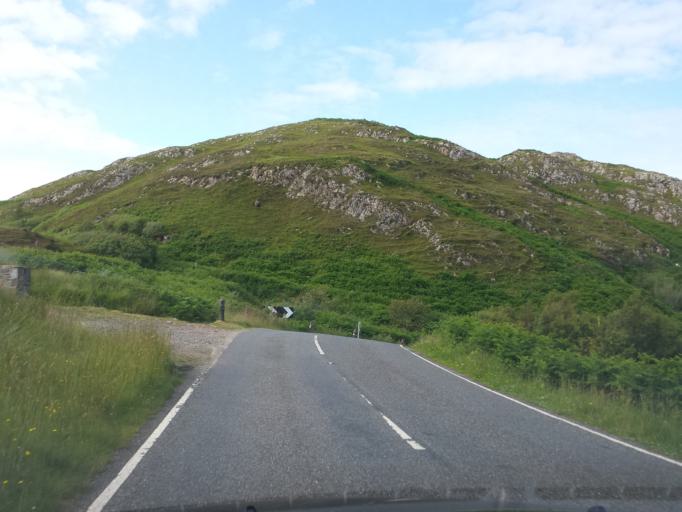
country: GB
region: Scotland
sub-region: Argyll and Bute
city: Isle Of Mull
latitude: 56.9591
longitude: -5.8413
